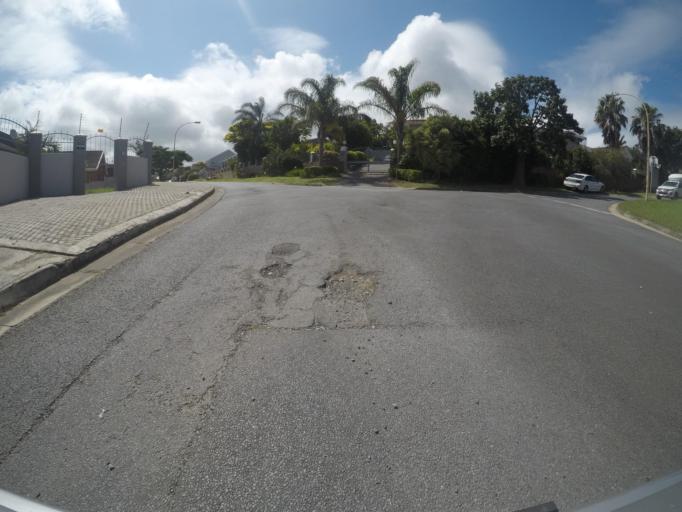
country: ZA
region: Eastern Cape
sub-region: Buffalo City Metropolitan Municipality
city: East London
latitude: -32.9994
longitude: 27.8880
